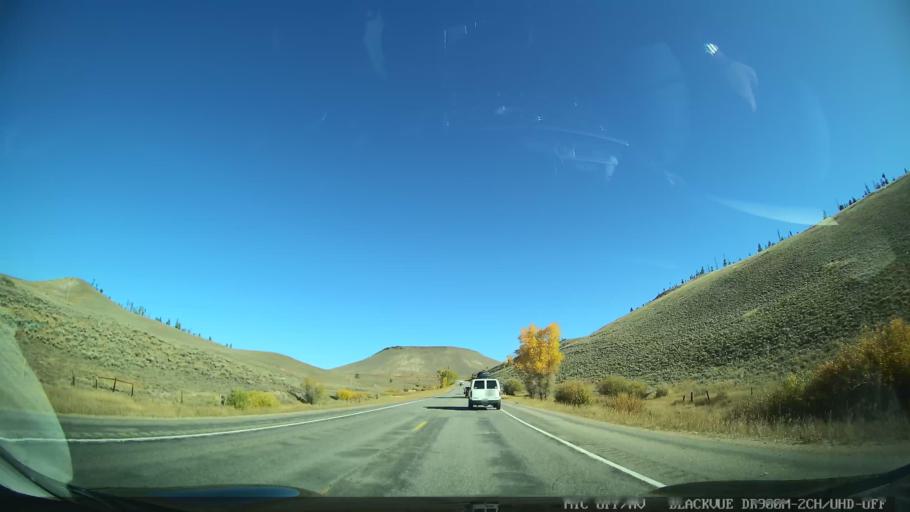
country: US
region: Colorado
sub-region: Grand County
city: Granby
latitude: 40.1274
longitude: -105.8968
